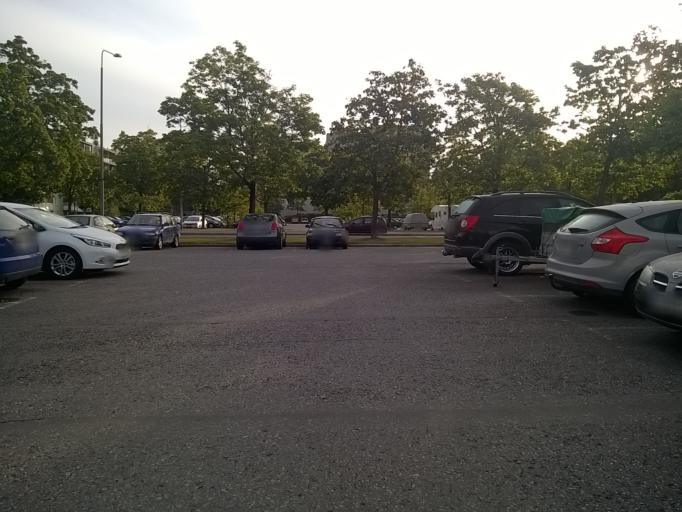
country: FI
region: Pirkanmaa
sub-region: Tampere
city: Tampere
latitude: 61.4453
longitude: 23.8476
